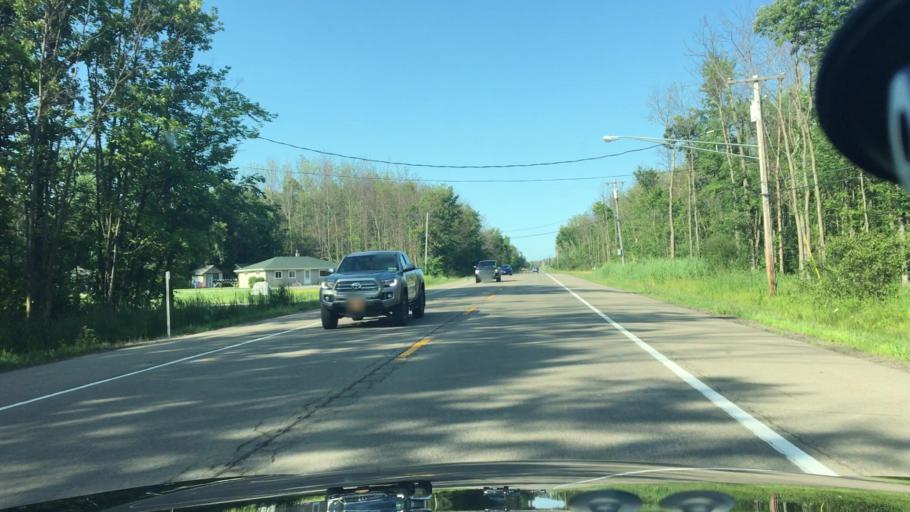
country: US
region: New York
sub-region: Erie County
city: Eden
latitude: 42.6691
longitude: -78.9619
